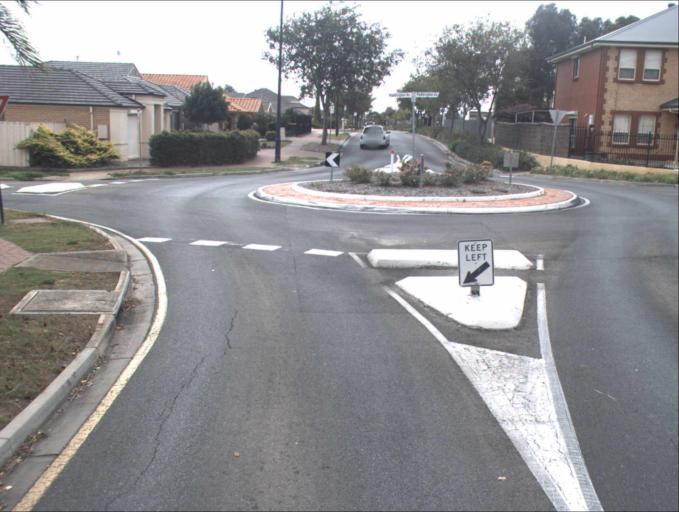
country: AU
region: South Australia
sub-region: Port Adelaide Enfield
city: Gilles Plains
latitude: -34.8561
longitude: 138.6325
